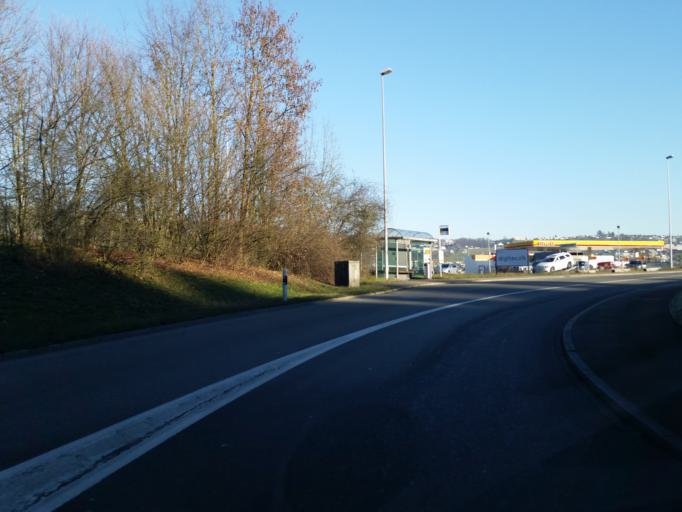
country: CH
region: Aargau
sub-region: Bezirk Bremgarten
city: Bremgarten
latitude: 47.3554
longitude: 8.3244
